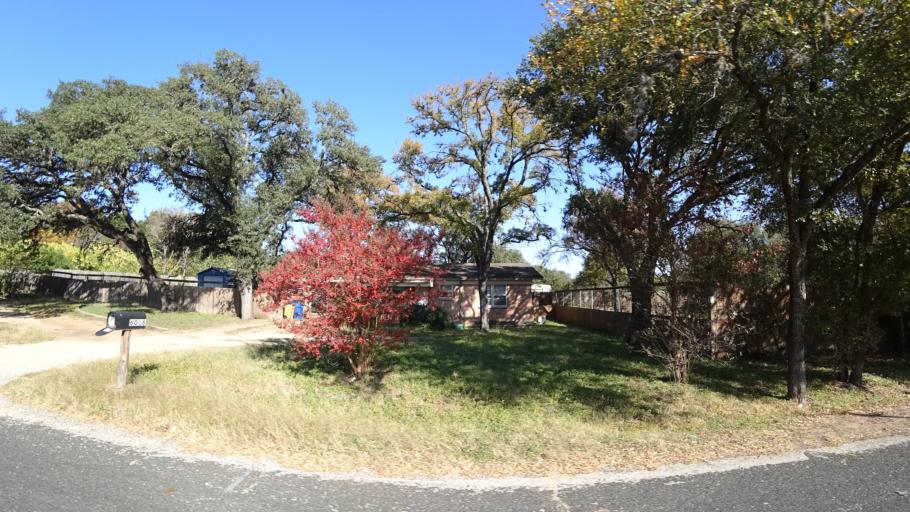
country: US
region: Texas
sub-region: Travis County
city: Barton Creek
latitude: 30.2340
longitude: -97.8483
